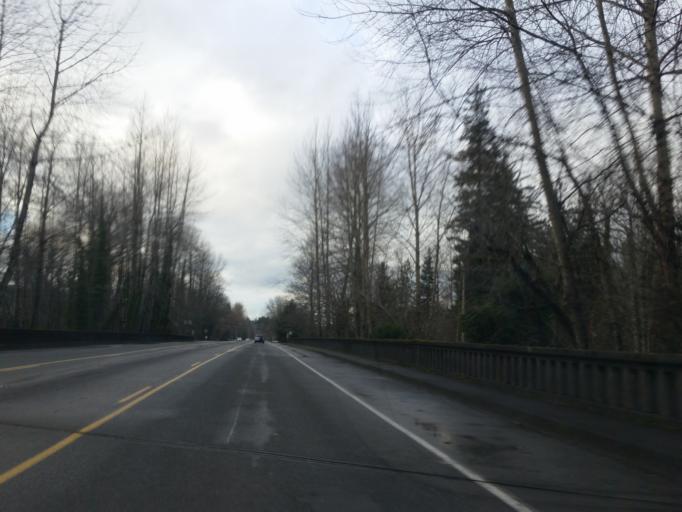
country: US
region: Washington
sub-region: King County
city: North Bend
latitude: 47.4971
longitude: -121.7902
